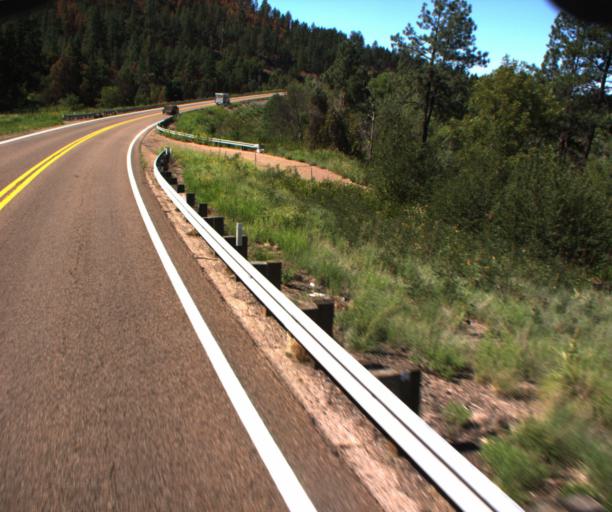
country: US
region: Arizona
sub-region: Navajo County
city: Linden
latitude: 34.0714
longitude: -110.1935
